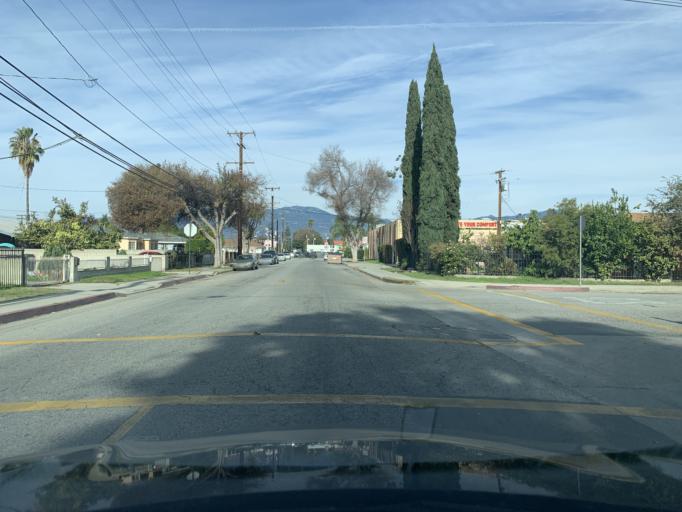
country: US
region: California
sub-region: Los Angeles County
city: South El Monte
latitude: 34.0612
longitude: -118.0557
